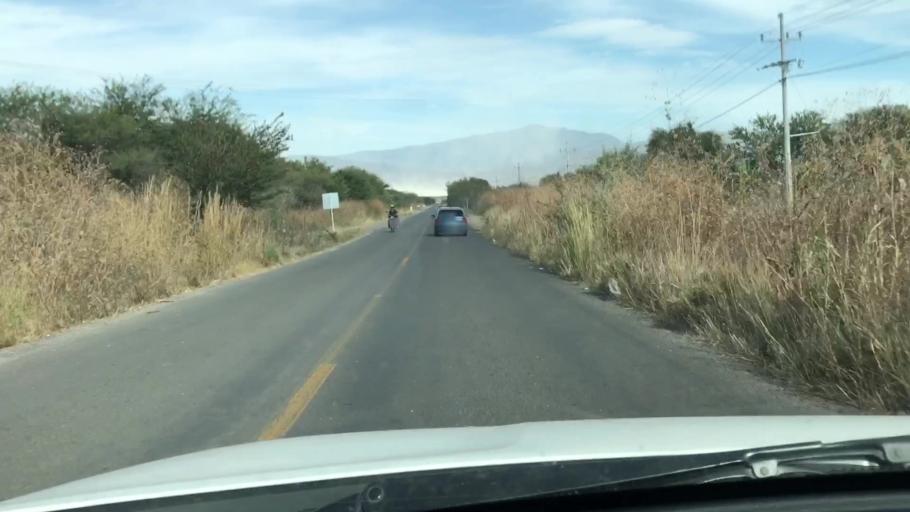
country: MX
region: Jalisco
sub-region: Zacoalco de Torres
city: Barranca de Otates (Barranca de Otatan)
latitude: 20.2770
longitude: -103.6279
